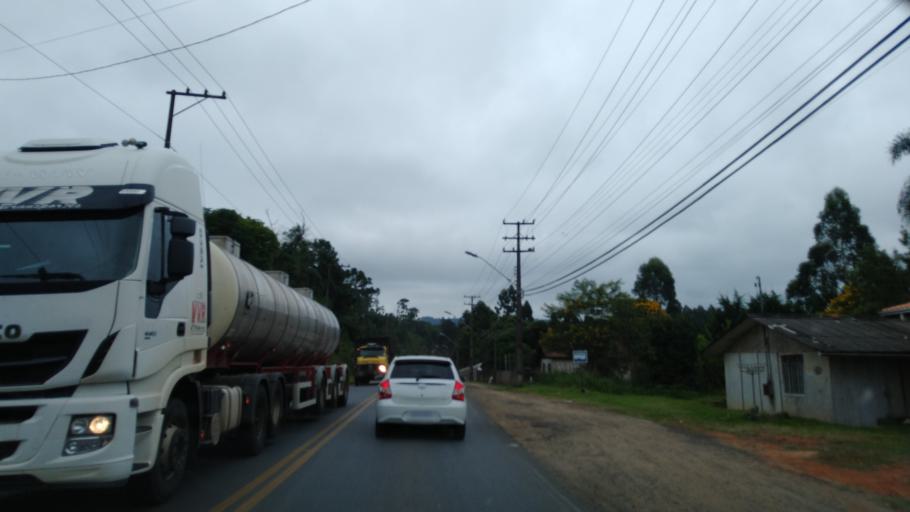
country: BR
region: Parana
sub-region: Uniao Da Vitoria
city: Uniao da Vitoria
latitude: -26.2504
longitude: -51.1187
